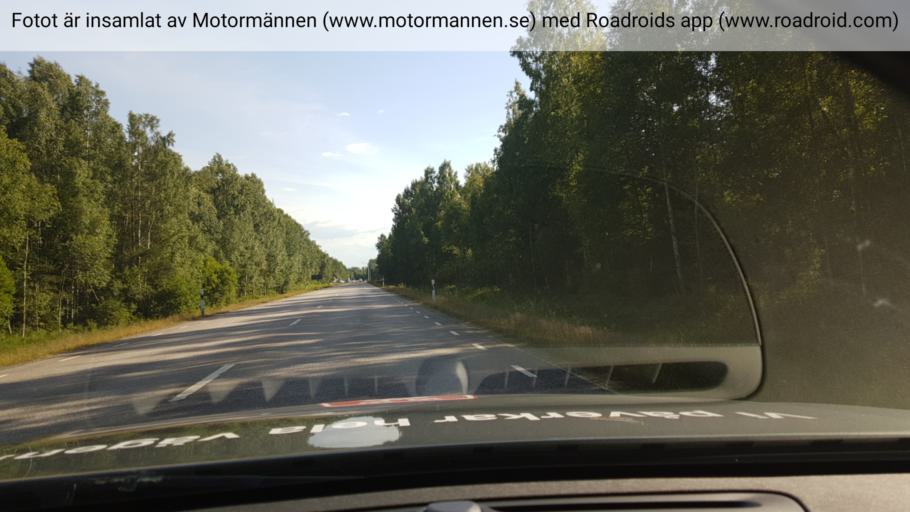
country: SE
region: Vaestra Goetaland
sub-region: Karlsborgs Kommun
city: Karlsborg
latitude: 58.5814
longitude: 14.4996
